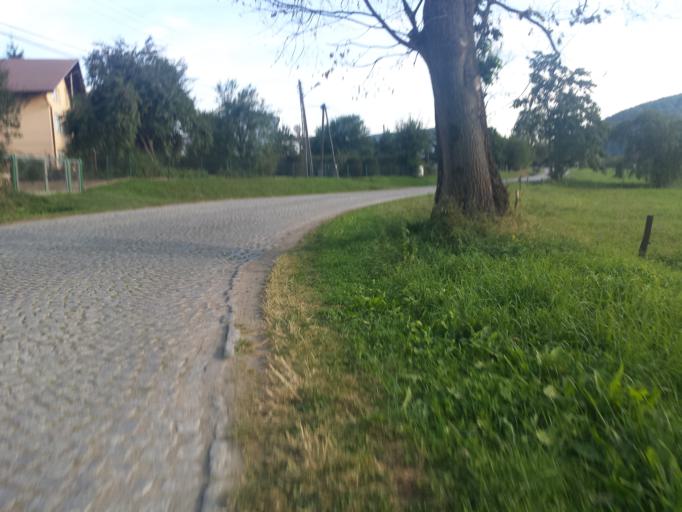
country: PL
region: Subcarpathian Voivodeship
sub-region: Powiat leski
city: Uherce Mineralne
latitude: 49.4393
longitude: 22.4105
